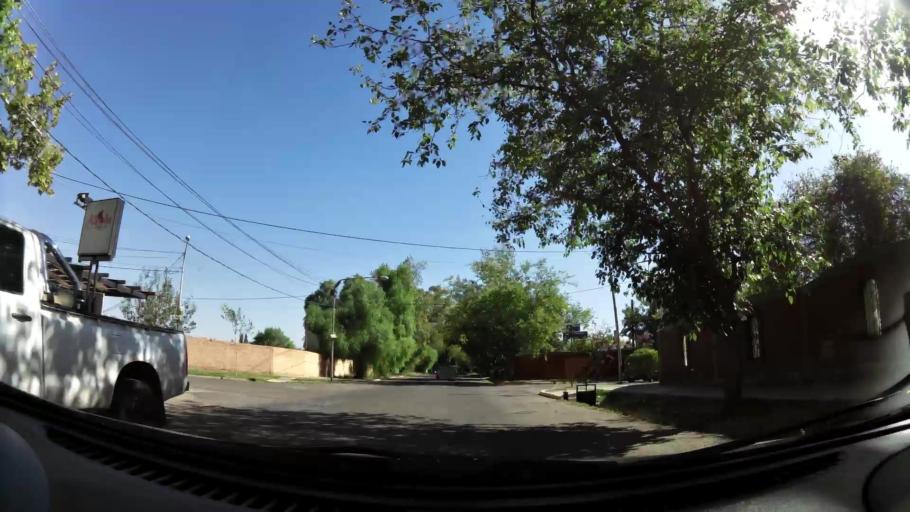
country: AR
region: Mendoza
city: Villa Nueva
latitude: -32.9103
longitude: -68.7922
